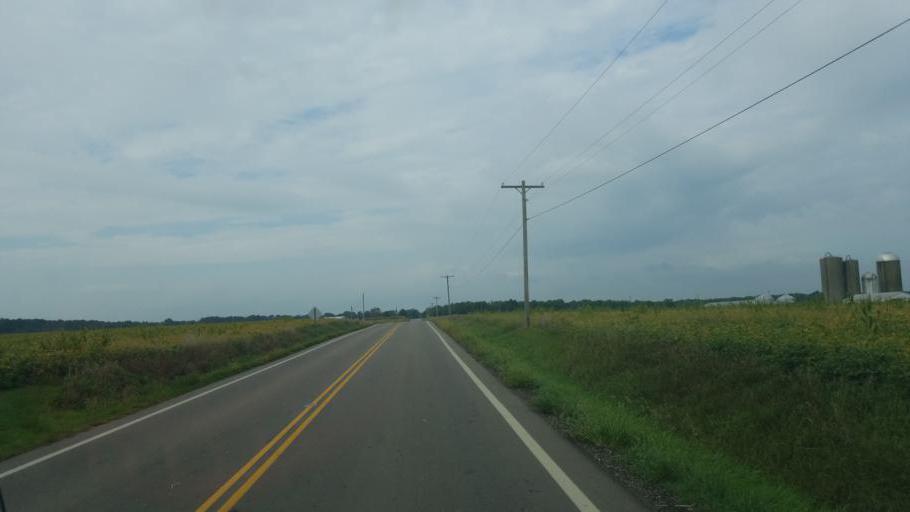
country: US
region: Ohio
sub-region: Wayne County
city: West Salem
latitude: 40.9093
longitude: -82.0513
